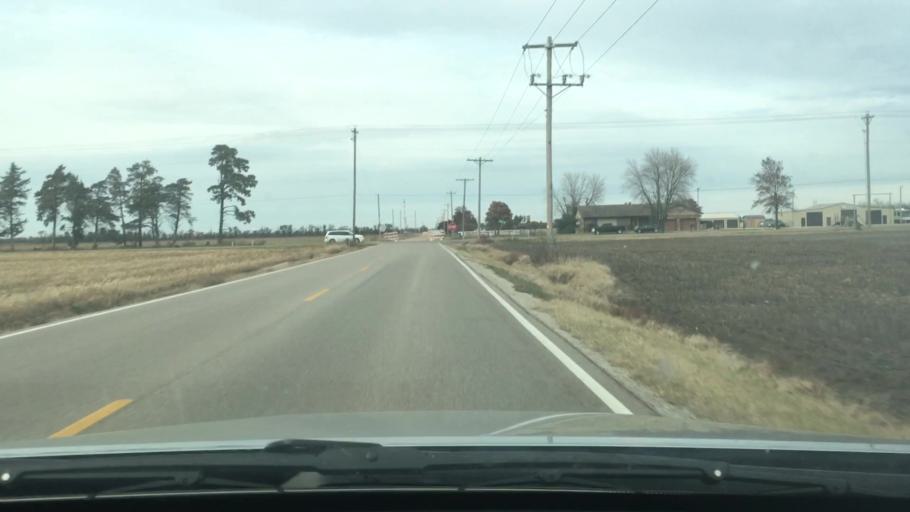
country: US
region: Kansas
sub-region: Sedgwick County
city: Maize
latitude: 37.7789
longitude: -97.4996
